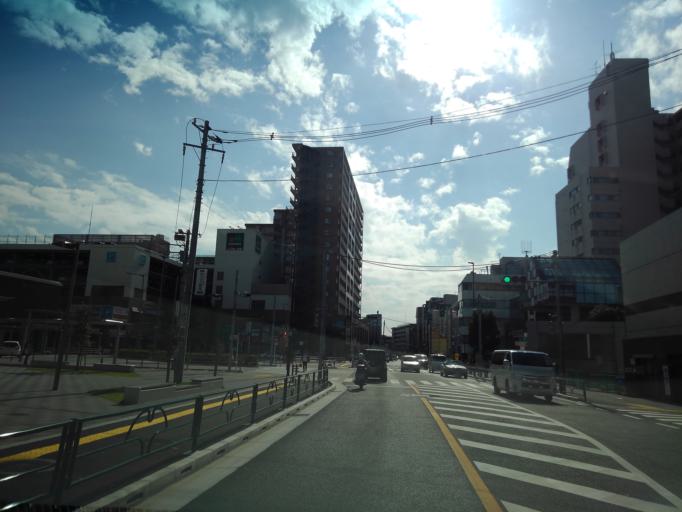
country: JP
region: Tokyo
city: Chofugaoka
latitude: 35.6502
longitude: 139.5574
